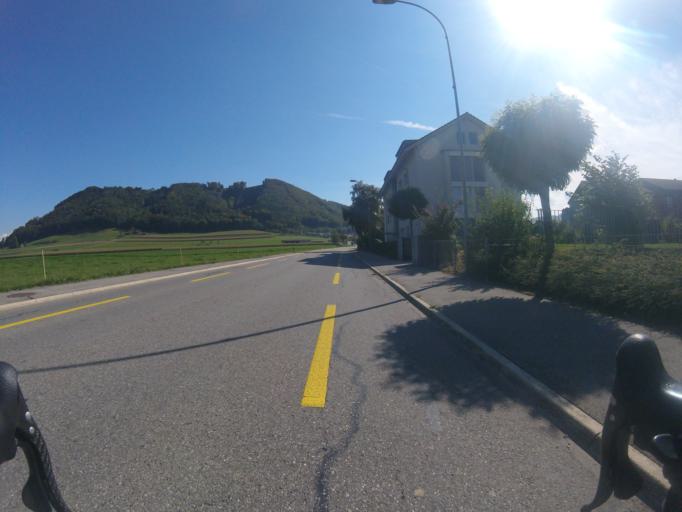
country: CH
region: Bern
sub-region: Bern-Mittelland District
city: Belp
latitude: 46.8884
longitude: 7.5028
